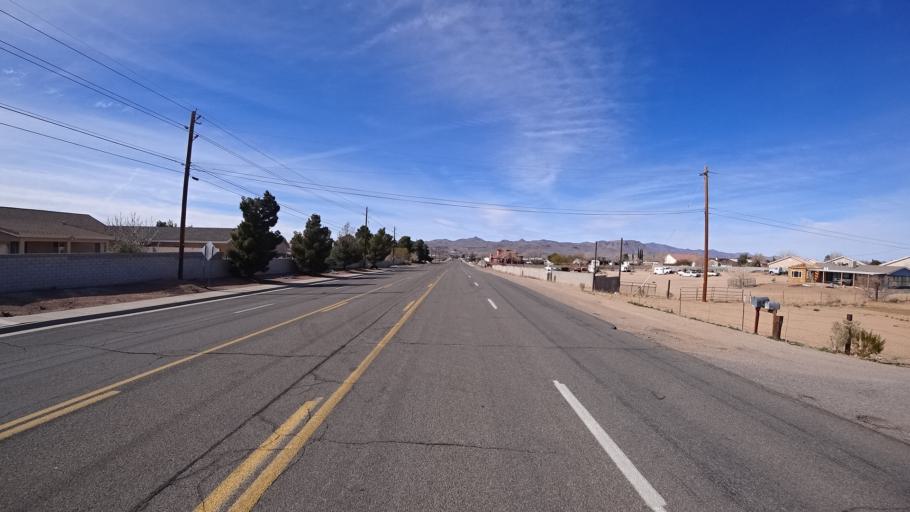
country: US
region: Arizona
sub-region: Mohave County
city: Kingman
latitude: 35.1874
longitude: -114.0088
